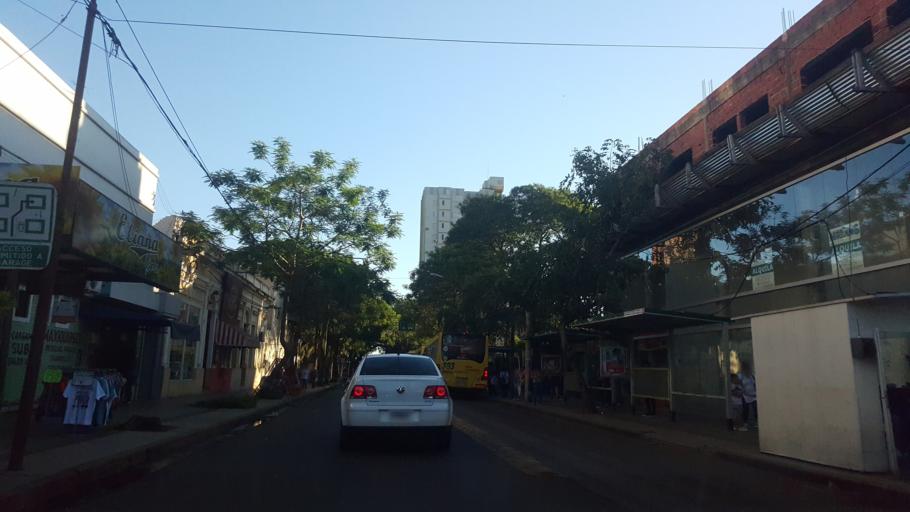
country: AR
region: Misiones
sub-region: Departamento de Capital
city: Posadas
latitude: -27.3675
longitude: -55.8979
